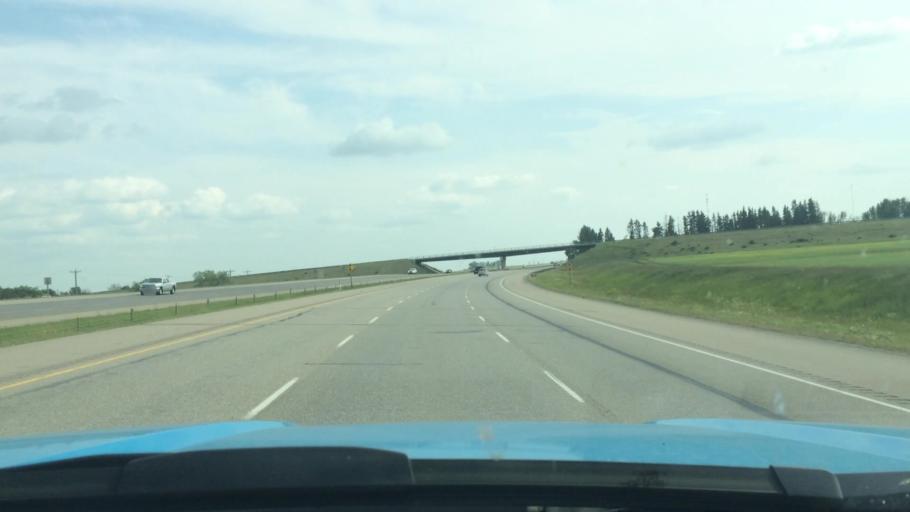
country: CA
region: Alberta
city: Crossfield
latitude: 51.4343
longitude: -114.0025
